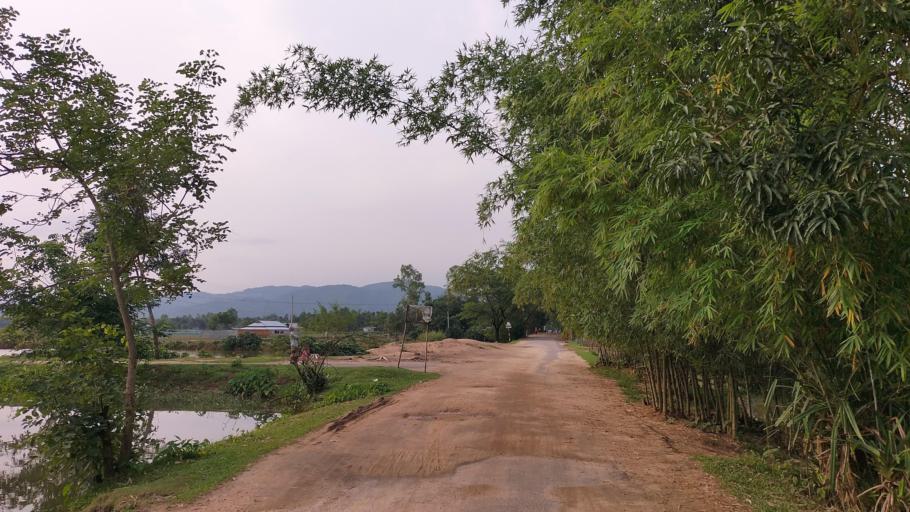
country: BD
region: Dhaka
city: Netrakona
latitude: 25.1322
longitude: 90.9132
